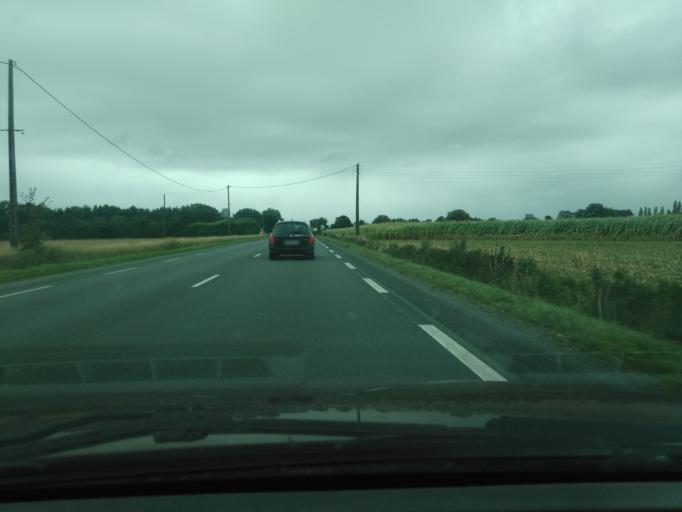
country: FR
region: Pays de la Loire
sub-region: Departement de la Vendee
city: Sainte-Gemme-la-Plaine
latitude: 46.4592
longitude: -1.1063
